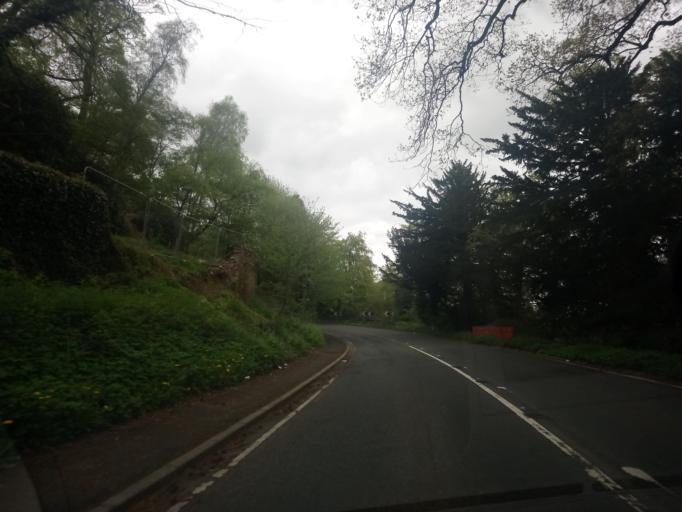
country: GB
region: England
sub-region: Telford and Wrekin
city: Newport
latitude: 52.7884
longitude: -2.3884
